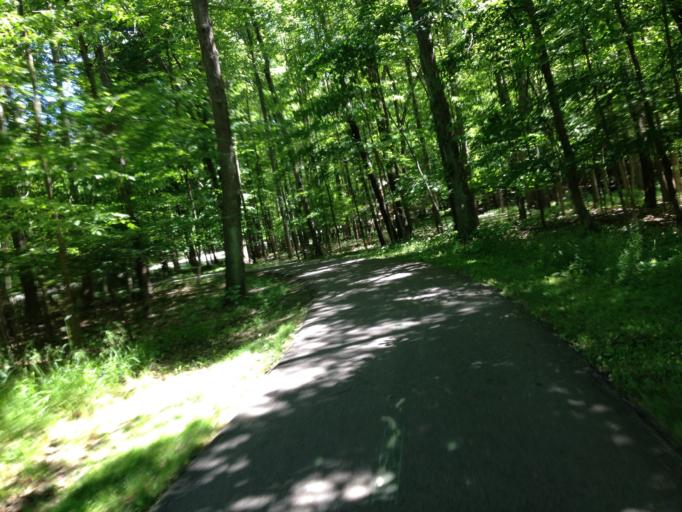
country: US
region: Ohio
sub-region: Cuyahoga County
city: Middleburg Heights
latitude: 41.3459
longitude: -81.8351
